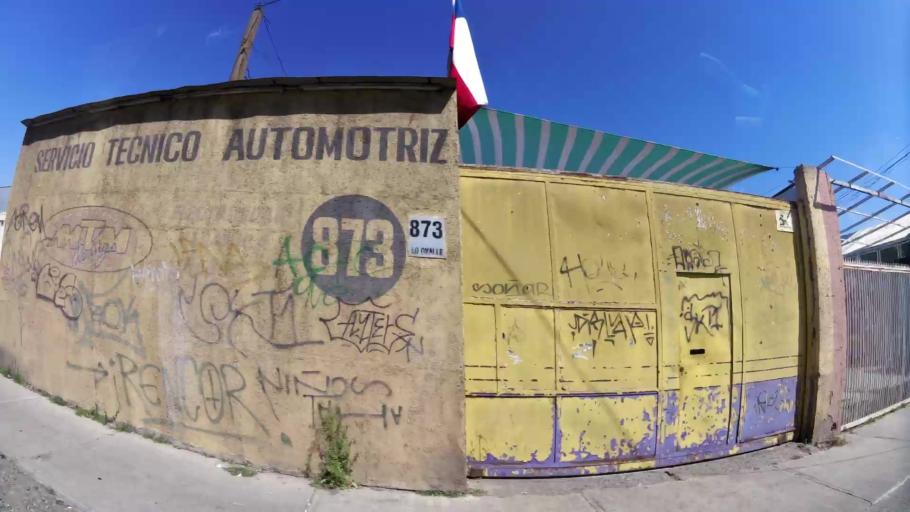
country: CL
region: Santiago Metropolitan
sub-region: Provincia de Santiago
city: Santiago
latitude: -33.5167
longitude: -70.6479
